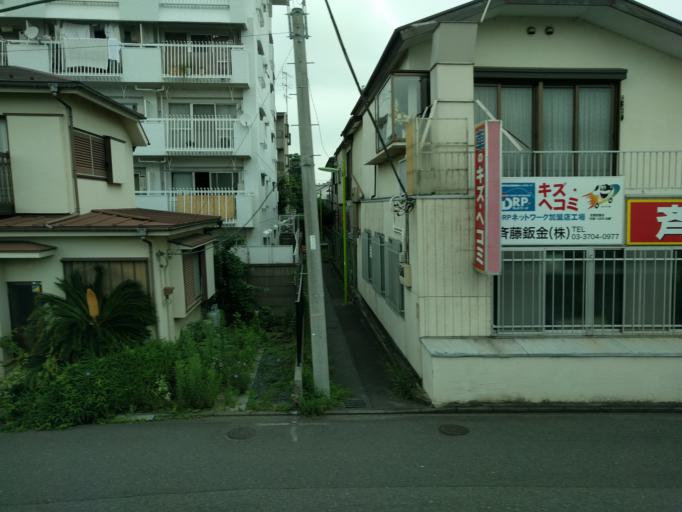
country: JP
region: Kanagawa
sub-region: Kawasaki-shi
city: Kawasaki
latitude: 35.5945
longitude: 139.6526
